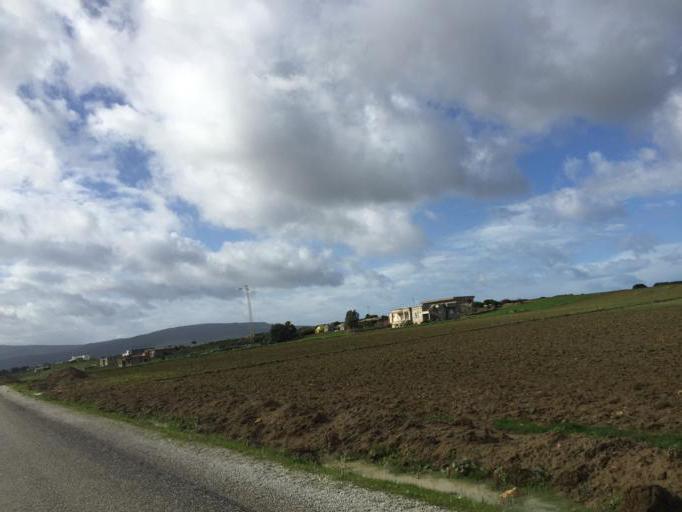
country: TN
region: Nabul
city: El Mida
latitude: 36.8853
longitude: 10.8569
